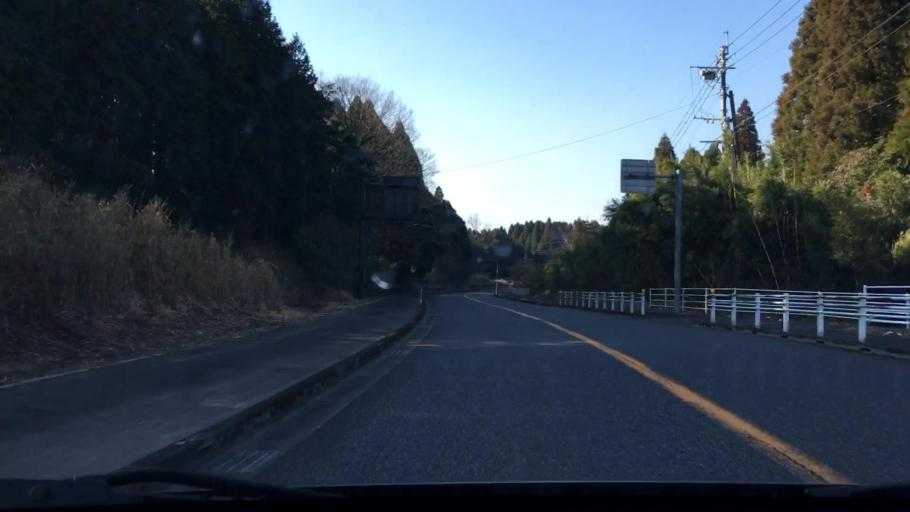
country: JP
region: Kagoshima
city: Sueyoshicho-ninokata
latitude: 31.6808
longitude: 130.9369
